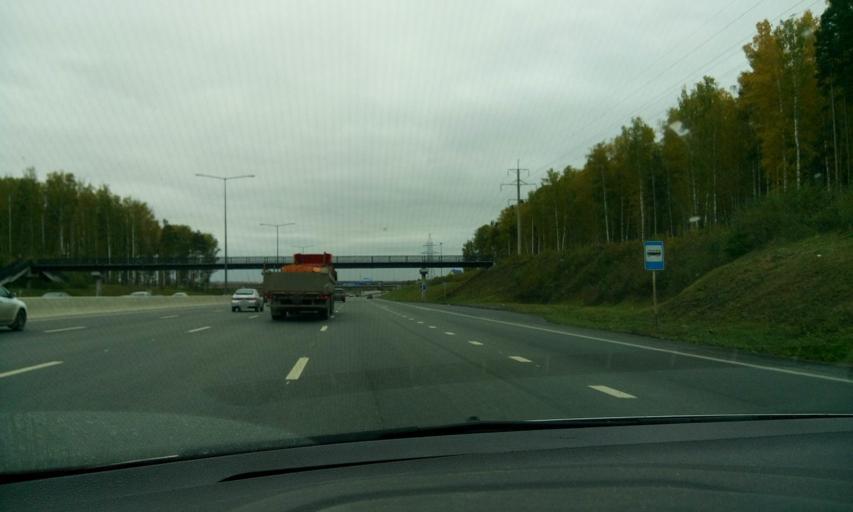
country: RU
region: Sverdlovsk
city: Istok
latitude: 56.7702
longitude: 60.7302
